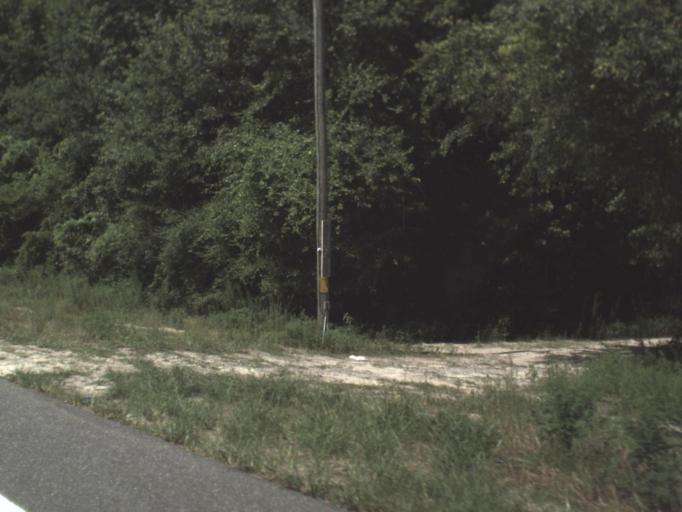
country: US
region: Florida
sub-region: Alachua County
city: High Springs
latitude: 29.8395
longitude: -82.7417
